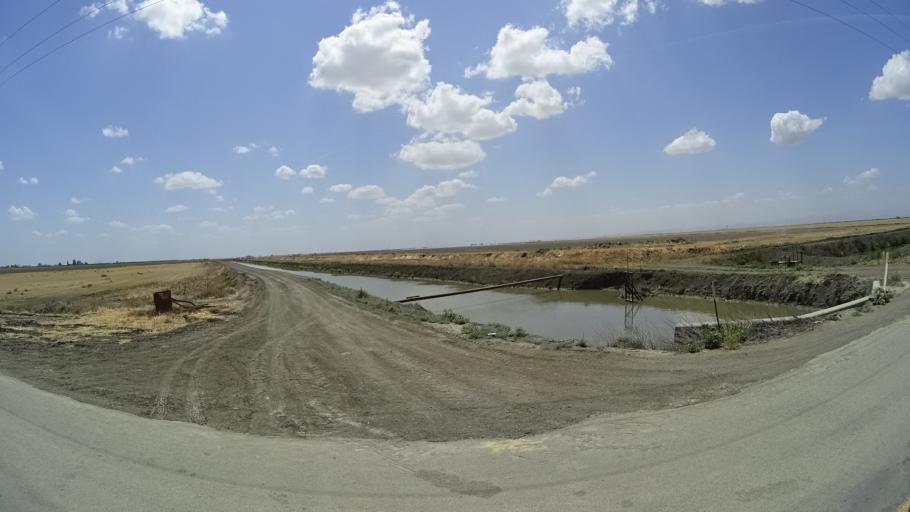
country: US
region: California
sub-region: Kings County
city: Stratford
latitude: 36.1895
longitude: -119.8717
